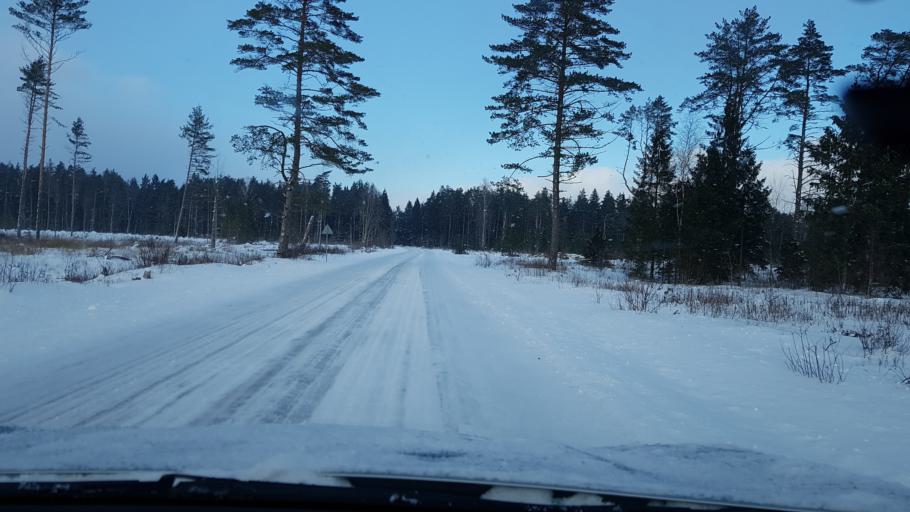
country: EE
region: Harju
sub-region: Nissi vald
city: Turba
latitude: 59.2060
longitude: 24.1406
